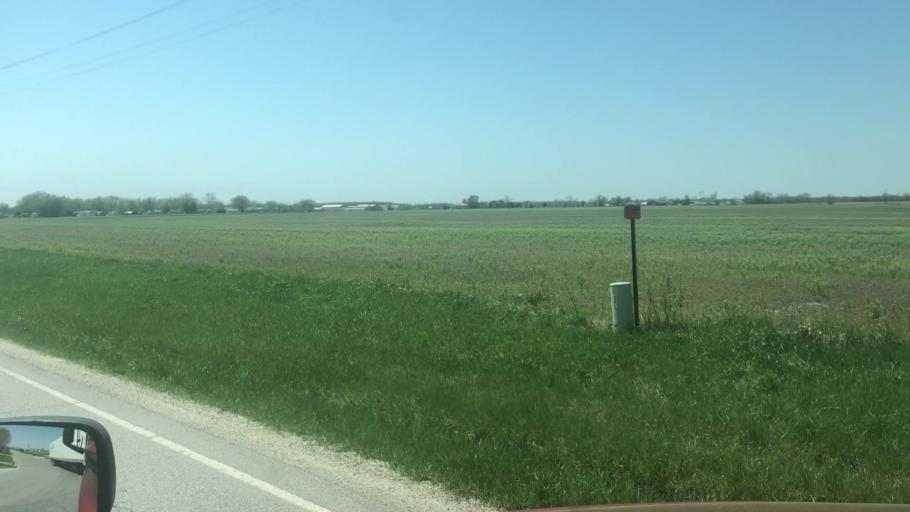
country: US
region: Missouri
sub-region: Adair County
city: Kirksville
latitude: 40.2210
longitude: -92.5922
